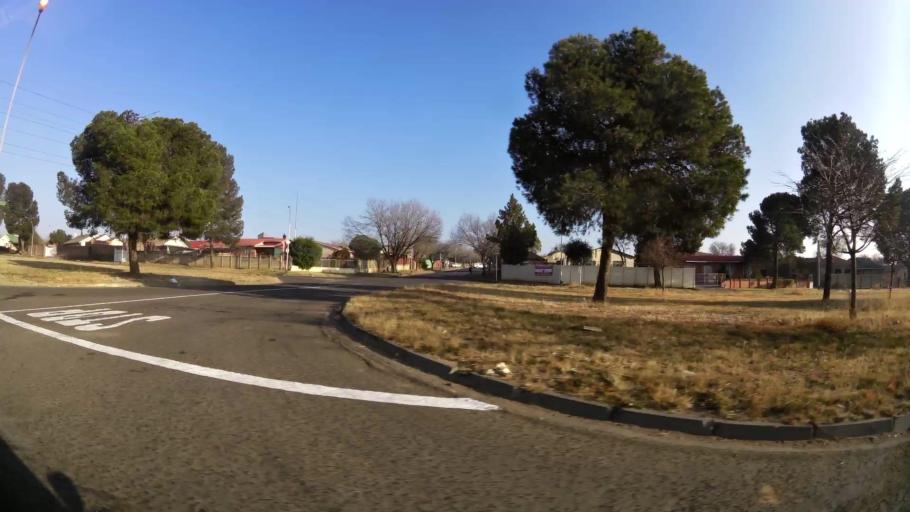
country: ZA
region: Orange Free State
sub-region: Mangaung Metropolitan Municipality
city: Bloemfontein
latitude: -29.1648
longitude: 26.2008
